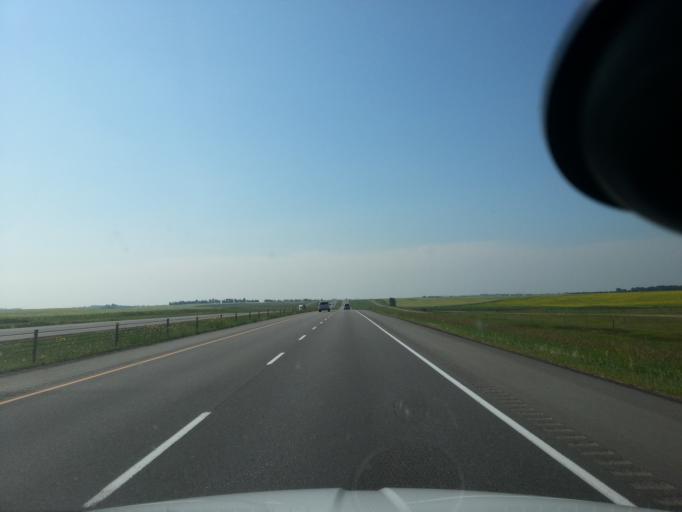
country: CA
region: Alberta
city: Carstairs
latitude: 51.6411
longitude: -114.0257
